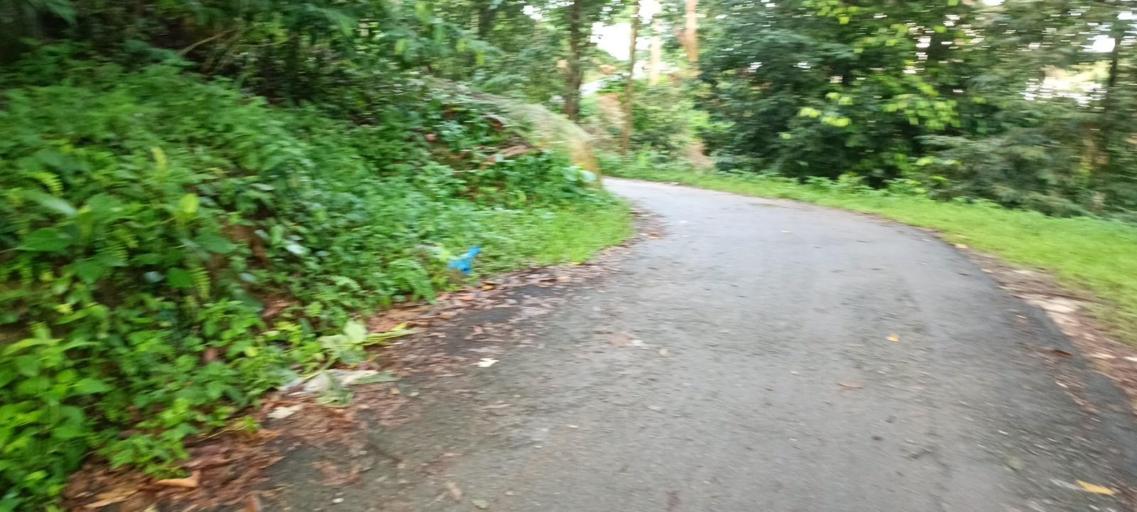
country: MY
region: Penang
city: Bukit Mertajam
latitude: 5.3742
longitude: 100.4765
